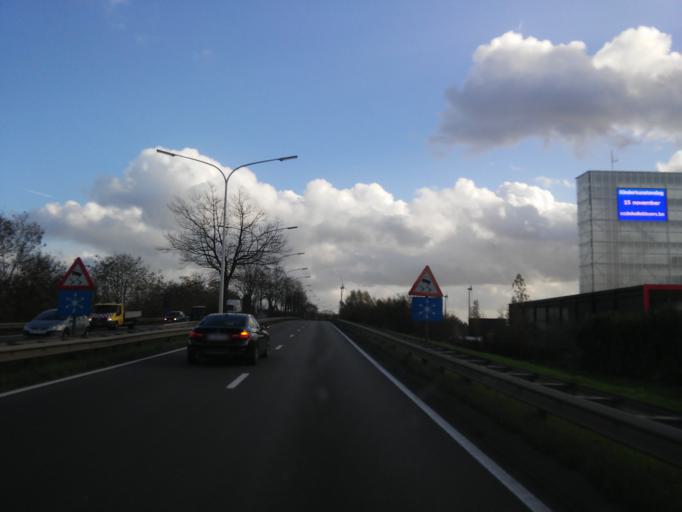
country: BE
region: Flanders
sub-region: Provincie Antwerpen
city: Puurs
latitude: 51.0780
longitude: 4.2969
